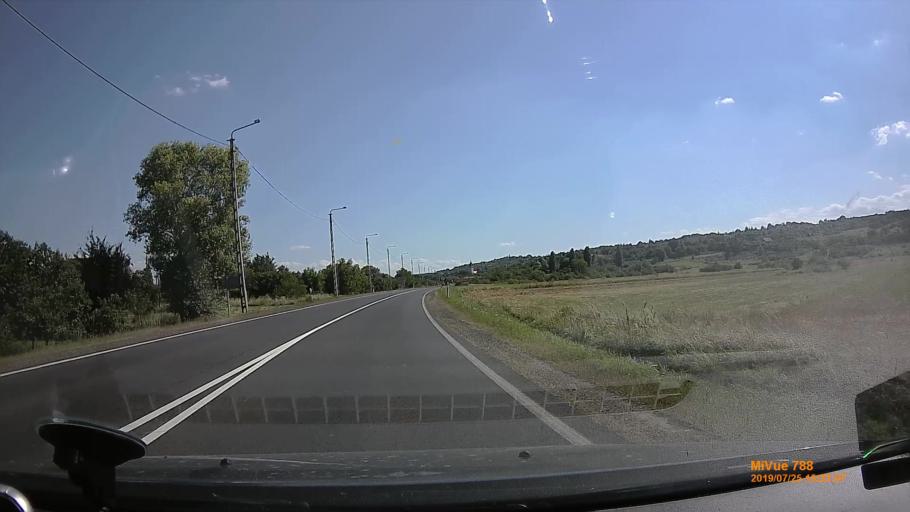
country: HU
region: Borsod-Abauj-Zemplen
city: Nyekladhaza
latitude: 47.9988
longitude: 20.8316
